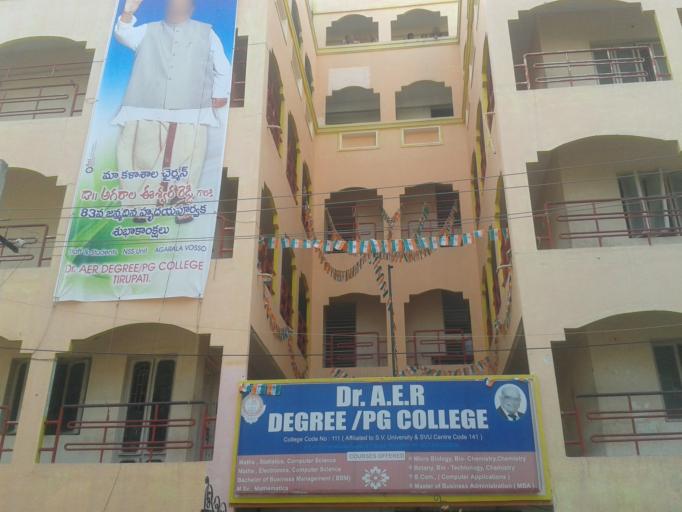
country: IN
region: Andhra Pradesh
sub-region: Chittoor
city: Akkarampalle
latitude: 13.6444
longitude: 79.4182
